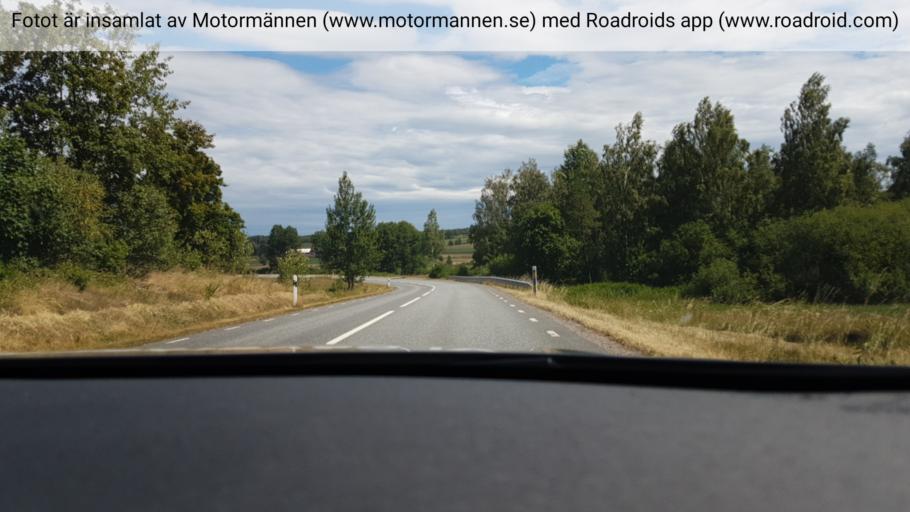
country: SE
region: Joenkoeping
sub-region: Aneby Kommun
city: Aneby
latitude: 57.9841
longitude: 14.8351
